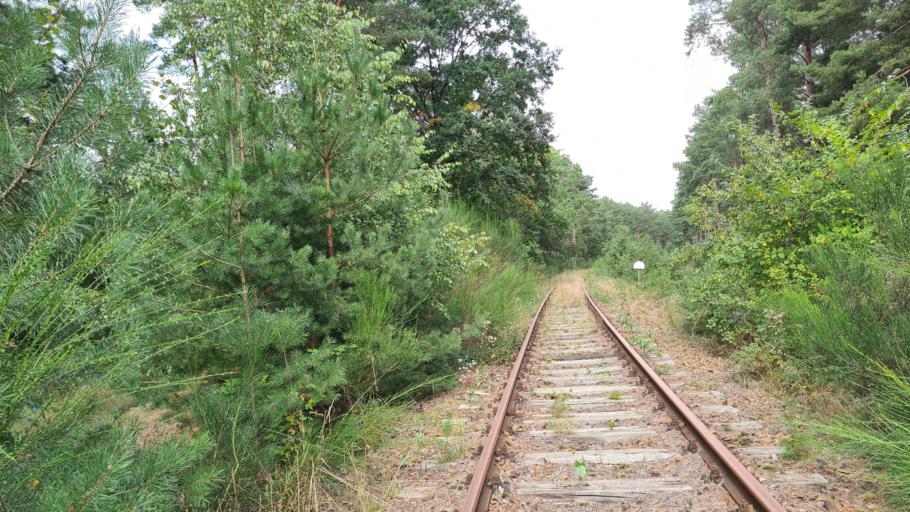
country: DE
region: Brandenburg
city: Crinitz
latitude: 51.7088
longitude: 13.7311
